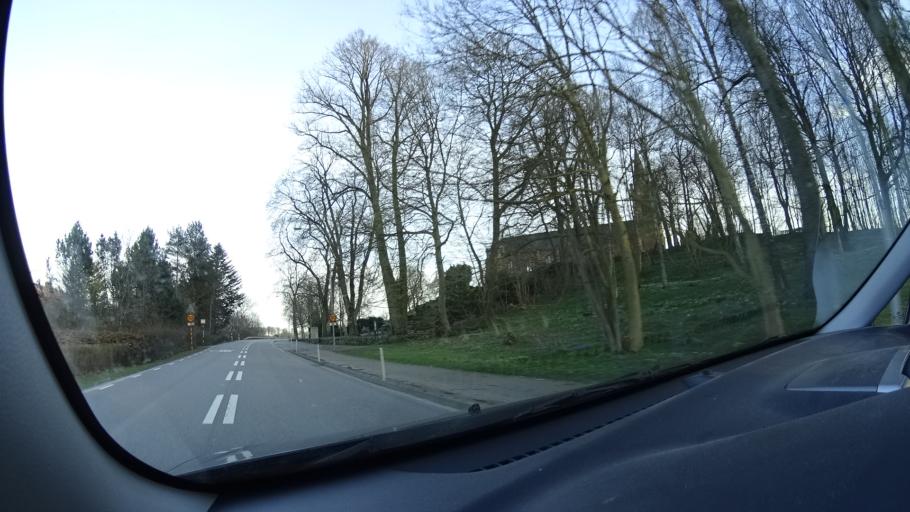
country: SE
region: Skane
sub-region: Eslovs Kommun
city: Stehag
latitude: 55.9604
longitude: 13.3345
